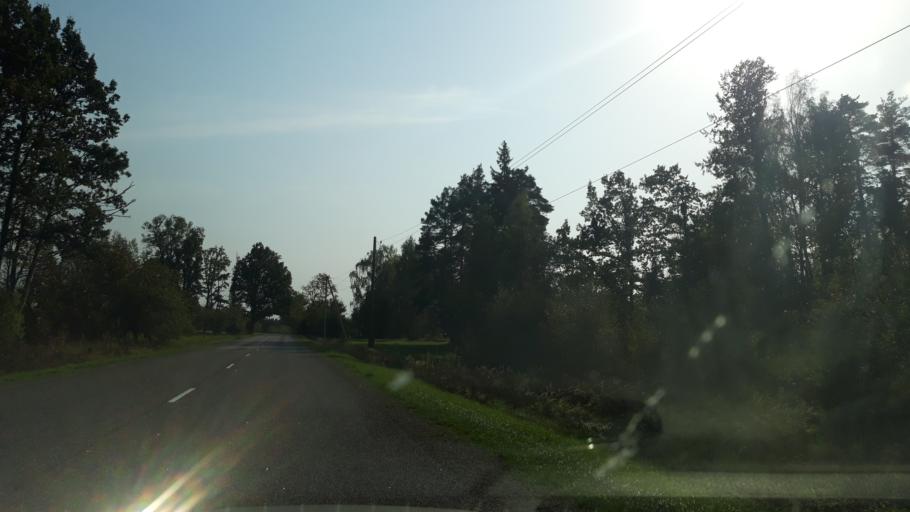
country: LV
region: Burtnieki
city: Matisi
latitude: 57.6279
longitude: 25.2663
